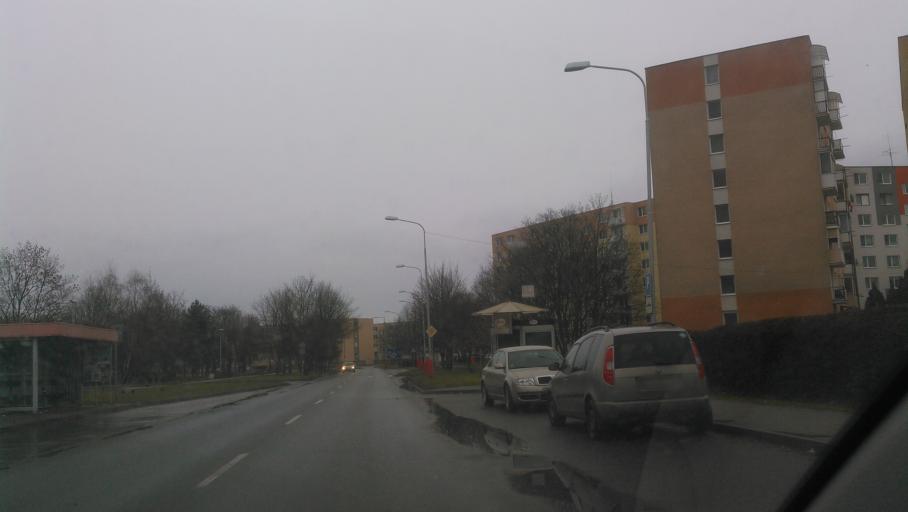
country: SK
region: Nitriansky
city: Sellye
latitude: 48.1473
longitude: 17.8766
